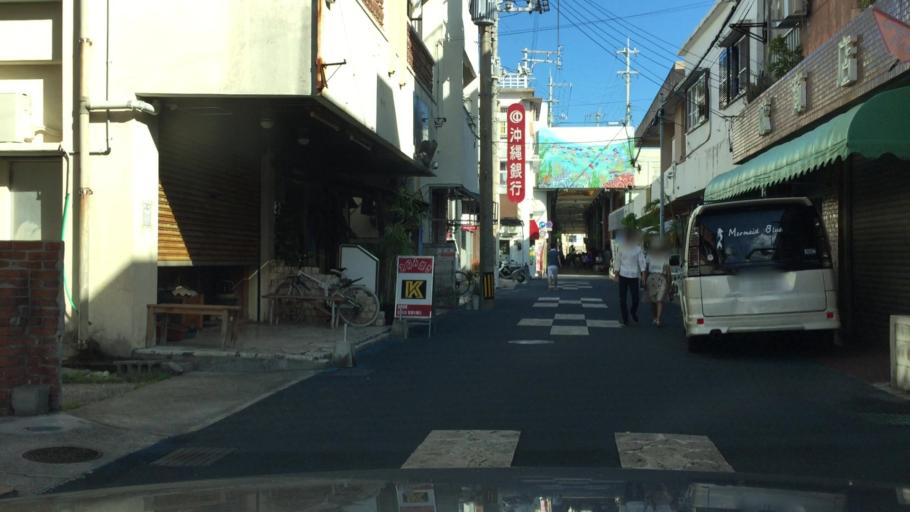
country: JP
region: Okinawa
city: Ishigaki
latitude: 24.3405
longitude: 124.1571
